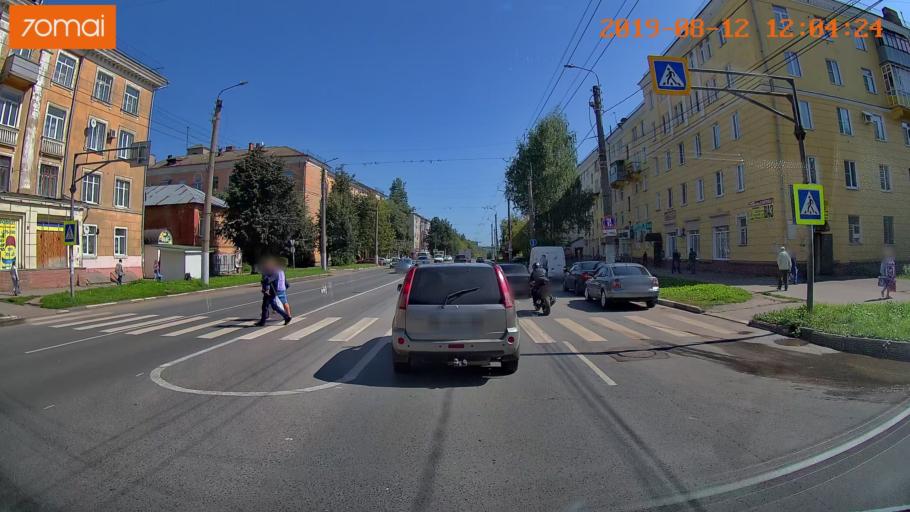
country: RU
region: Ivanovo
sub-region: Gorod Ivanovo
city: Ivanovo
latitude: 56.9945
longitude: 41.0040
